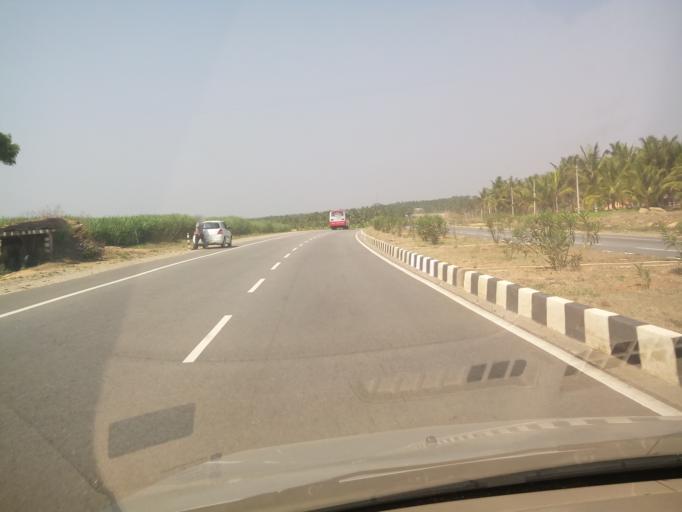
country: IN
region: Karnataka
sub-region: Hassan
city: Shravanabelagola
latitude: 12.9176
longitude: 76.4656
